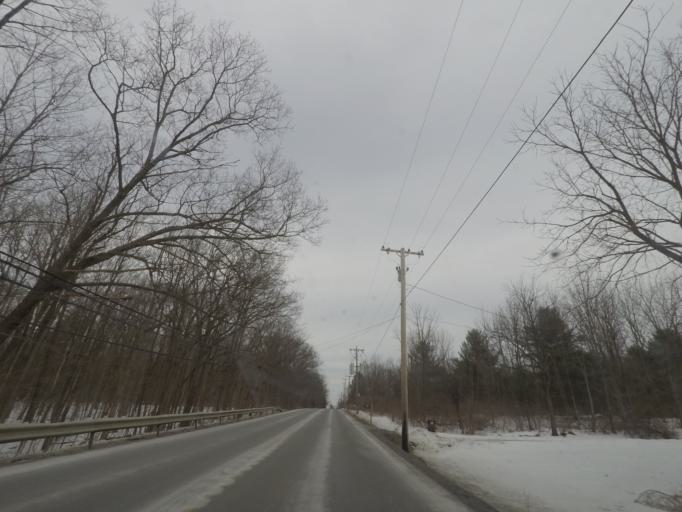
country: US
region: New York
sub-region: Albany County
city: Voorheesville
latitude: 42.5754
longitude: -73.9409
